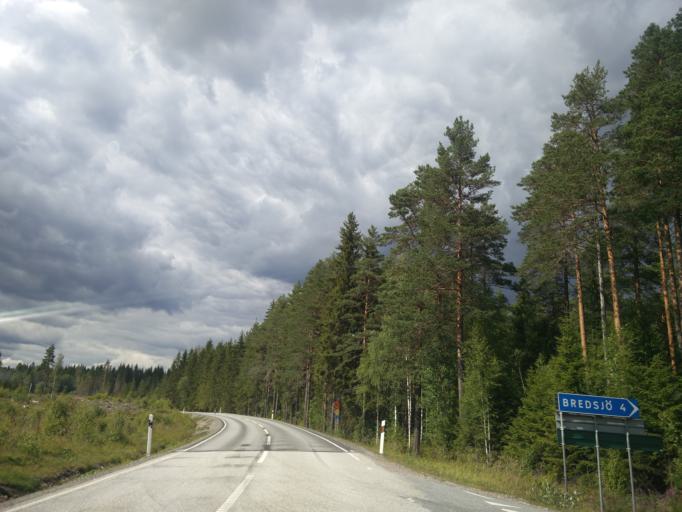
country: SE
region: OErebro
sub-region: Hallefors Kommun
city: Haellefors
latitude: 59.8098
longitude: 14.6938
